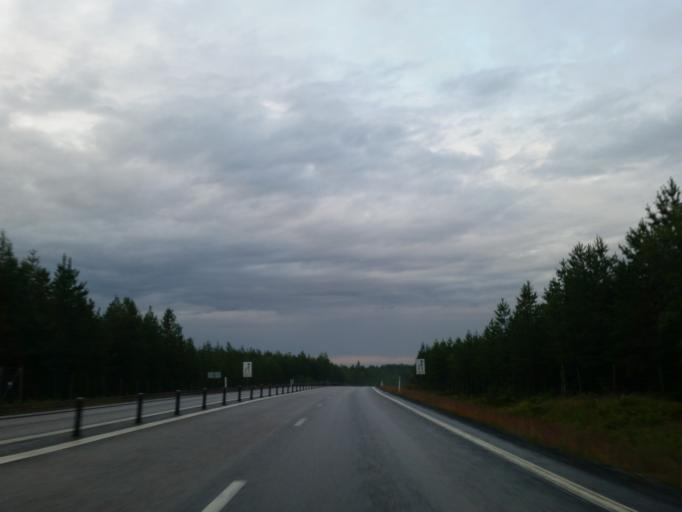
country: SE
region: Vaesterbotten
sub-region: Umea Kommun
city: Saevar
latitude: 63.9846
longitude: 20.7342
